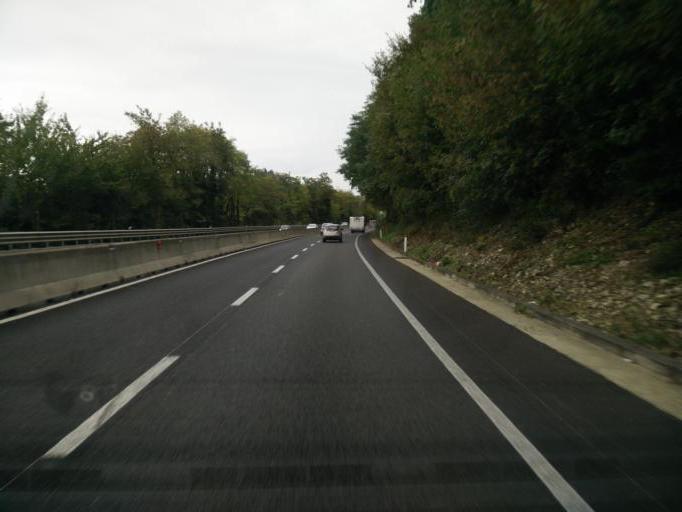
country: IT
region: Tuscany
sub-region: Province of Florence
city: San Casciano in Val di Pesa
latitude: 43.6478
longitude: 11.1822
